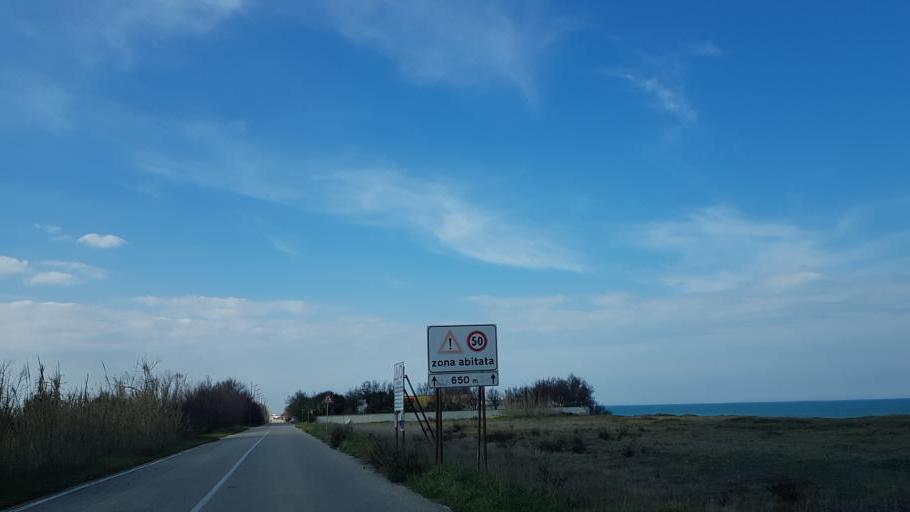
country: IT
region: Apulia
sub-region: Provincia di Brindisi
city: Brindisi
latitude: 40.6903
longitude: 17.8392
